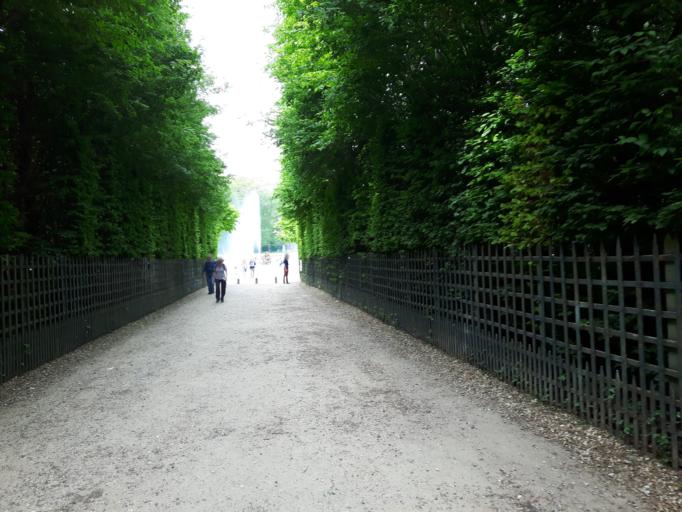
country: FR
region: Ile-de-France
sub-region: Departement des Yvelines
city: Le Chesnay
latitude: 48.8078
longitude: 2.1122
